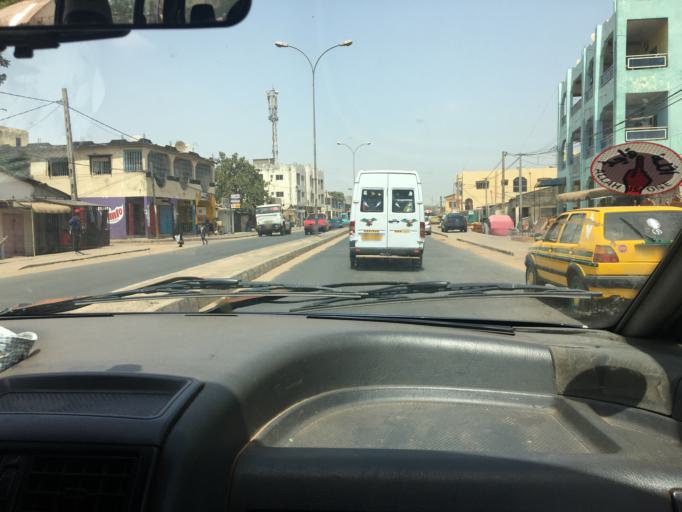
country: GM
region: Western
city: Abuko
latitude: 13.4098
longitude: -16.6689
